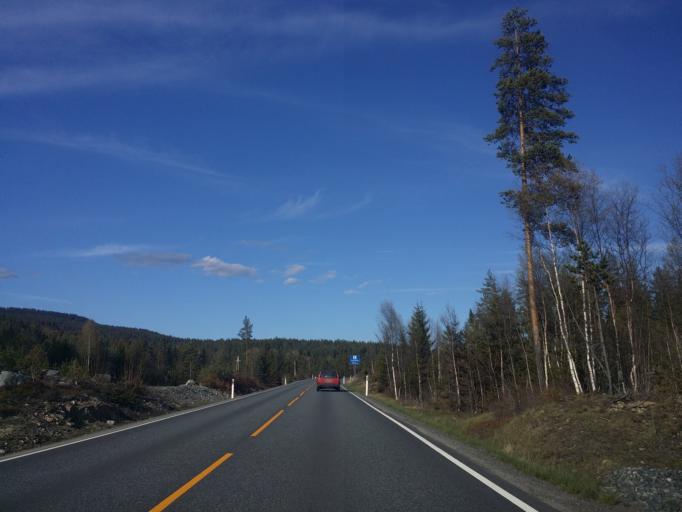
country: NO
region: Buskerud
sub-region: Kongsberg
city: Kongsberg
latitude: 59.6320
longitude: 9.5157
